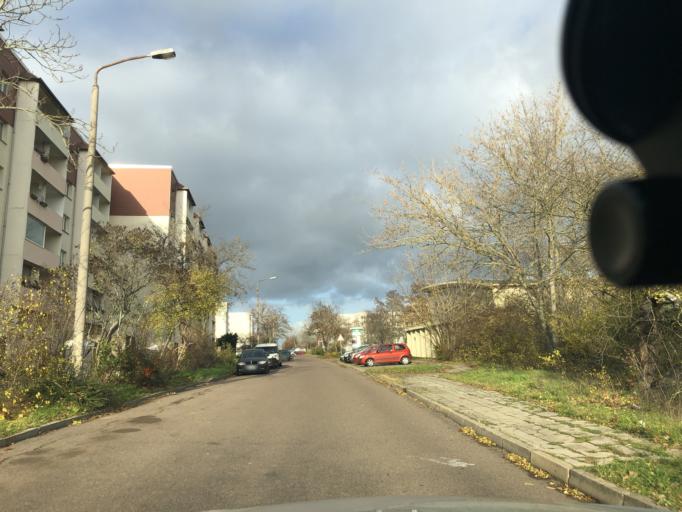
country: DE
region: Saxony-Anhalt
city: Halle Neustadt
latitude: 51.4740
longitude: 11.9082
